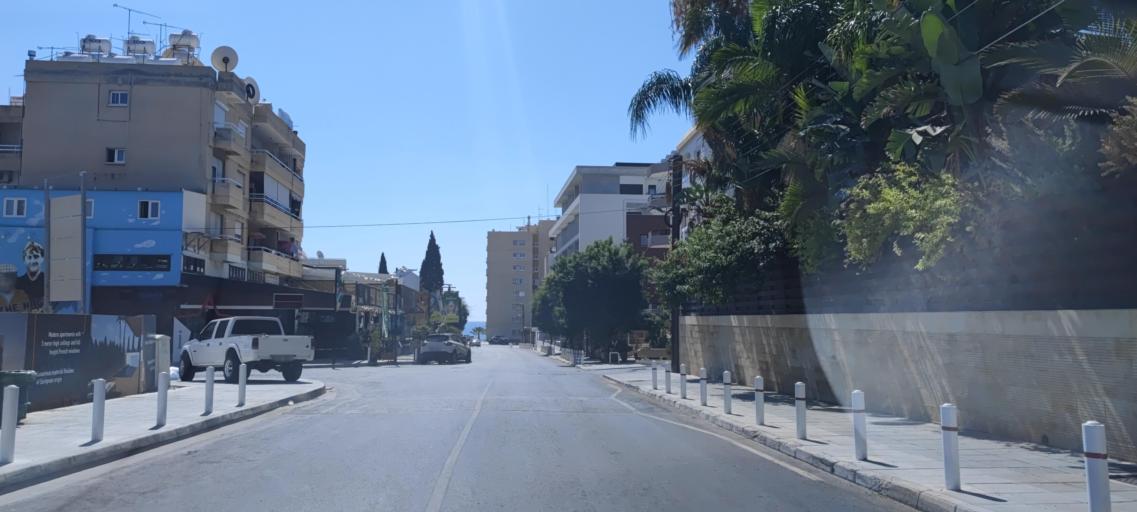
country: CY
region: Limassol
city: Mouttagiaka
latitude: 34.7009
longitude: 33.0988
